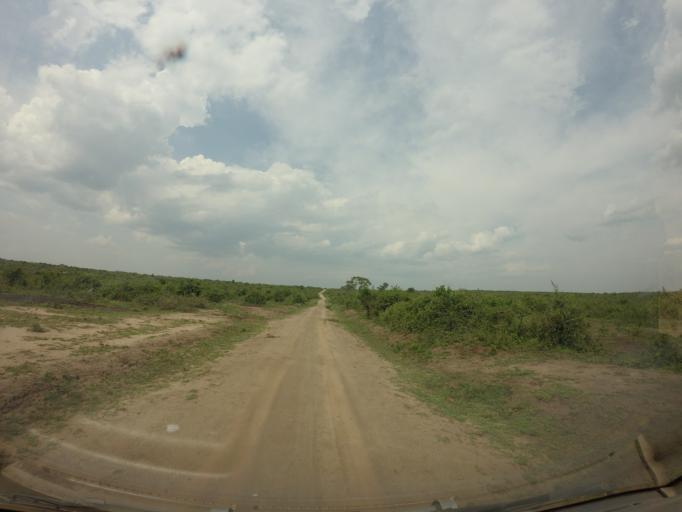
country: UG
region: Western Region
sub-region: Rubirizi District
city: Rubirizi
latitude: -0.2100
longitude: 29.9119
